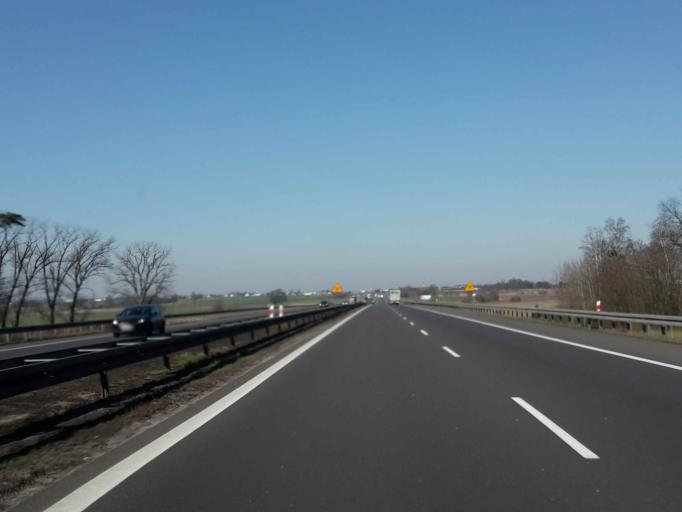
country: PL
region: Greater Poland Voivodeship
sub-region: Powiat poznanski
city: Swarzedz
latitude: 52.3376
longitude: 17.0508
